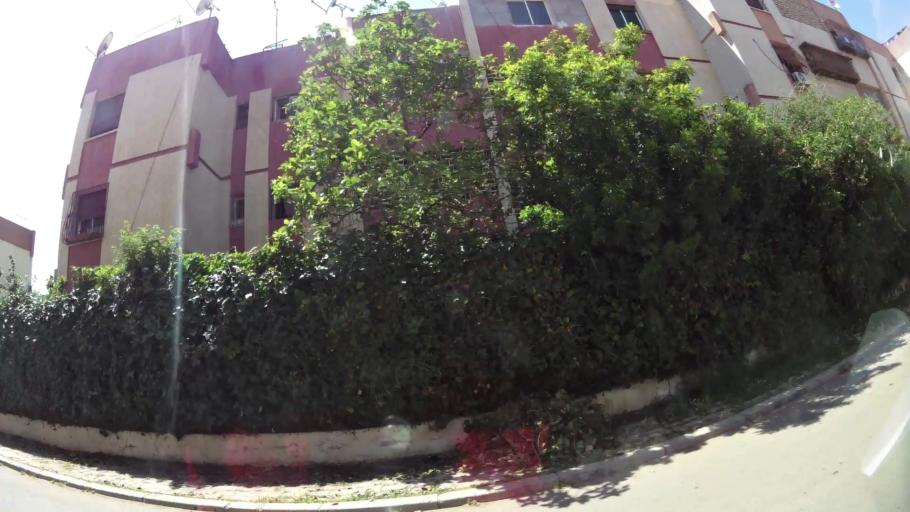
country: MA
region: Rabat-Sale-Zemmour-Zaer
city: Sale
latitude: 34.0443
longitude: -6.7934
